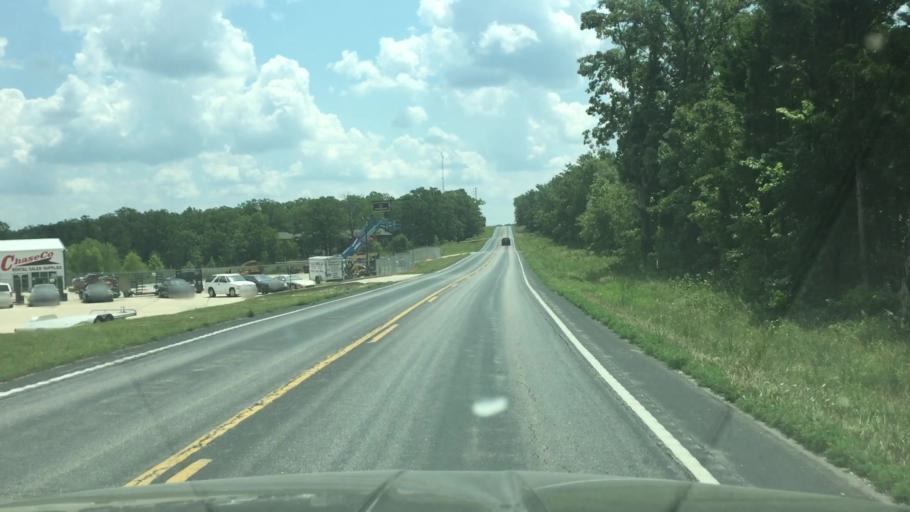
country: US
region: Missouri
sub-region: Camden County
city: Osage Beach
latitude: 38.1392
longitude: -92.5805
